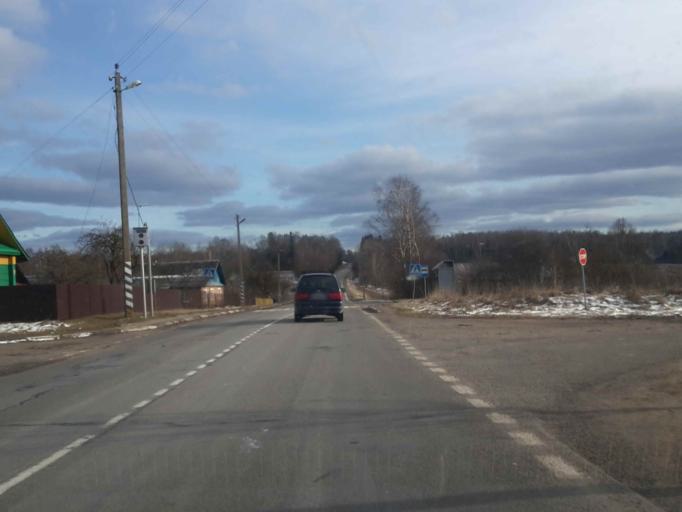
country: BY
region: Minsk
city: Il'ya
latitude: 54.2837
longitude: 27.4878
